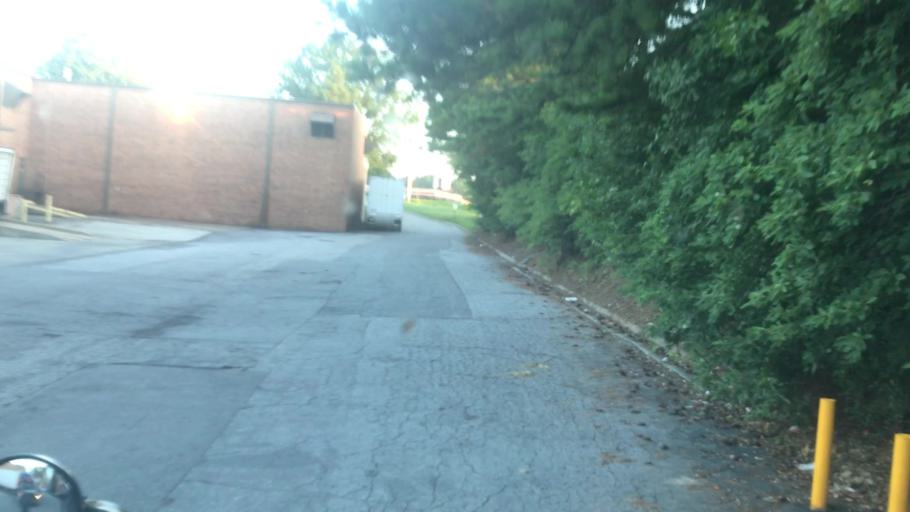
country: US
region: Georgia
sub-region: DeKalb County
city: Doraville
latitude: 33.9284
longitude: -84.2641
